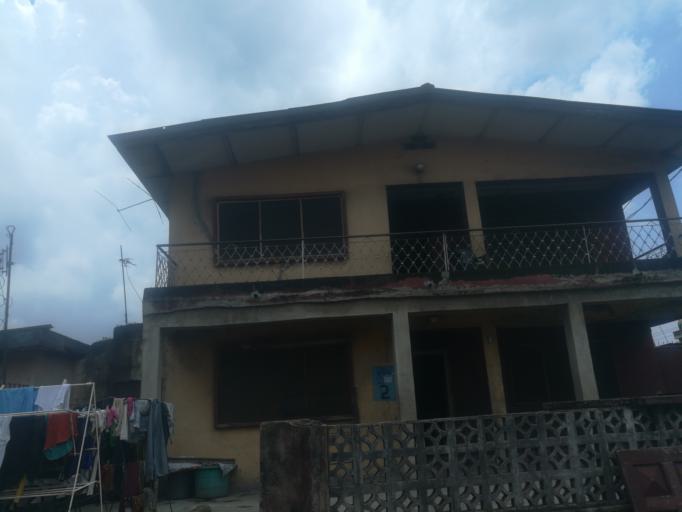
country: NG
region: Lagos
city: Somolu
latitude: 6.5514
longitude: 3.3916
